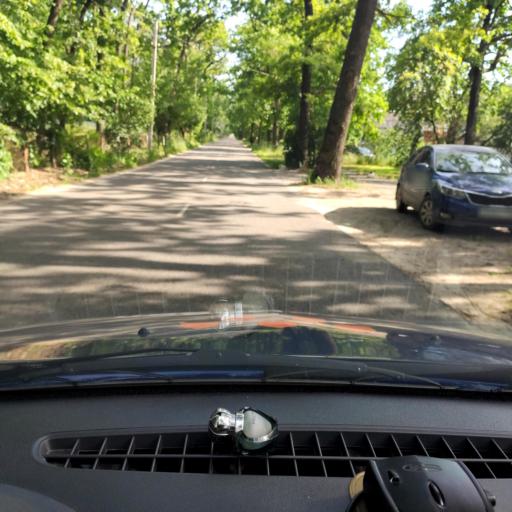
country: RU
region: Voronezj
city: Somovo
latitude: 51.7513
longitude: 39.3661
